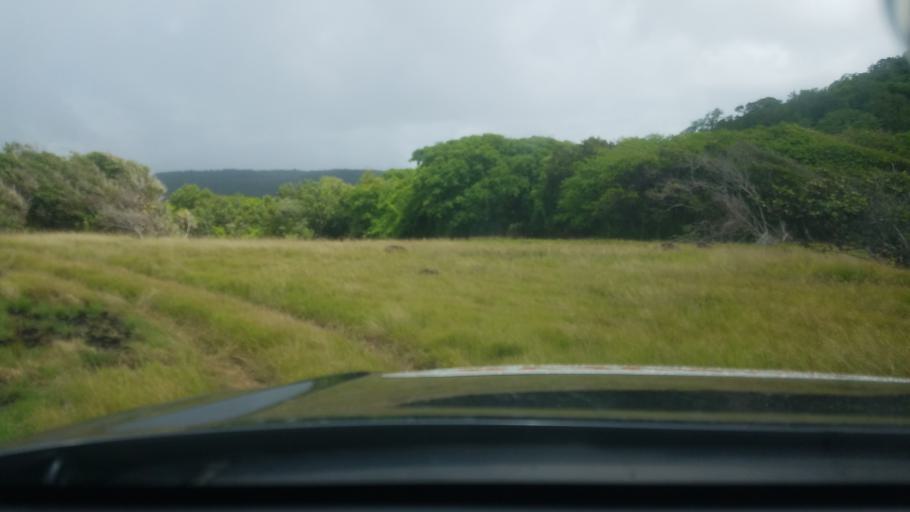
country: LC
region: Praslin
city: Praslin
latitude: 13.8691
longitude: -60.8862
